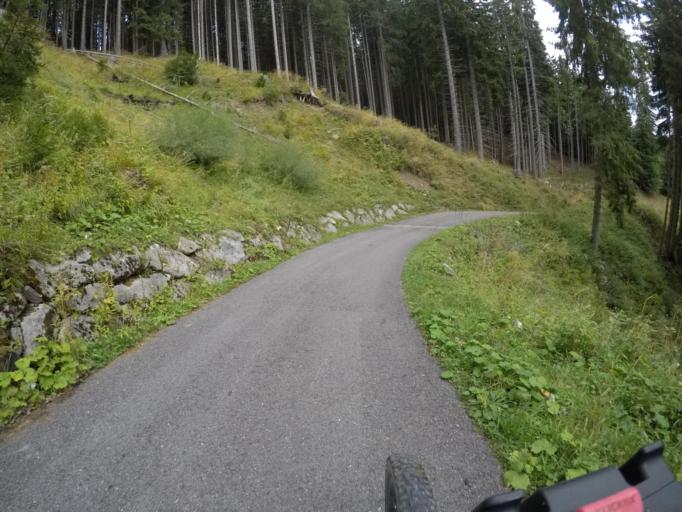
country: IT
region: Friuli Venezia Giulia
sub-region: Provincia di Udine
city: Pontebba
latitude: 46.5142
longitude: 13.2469
